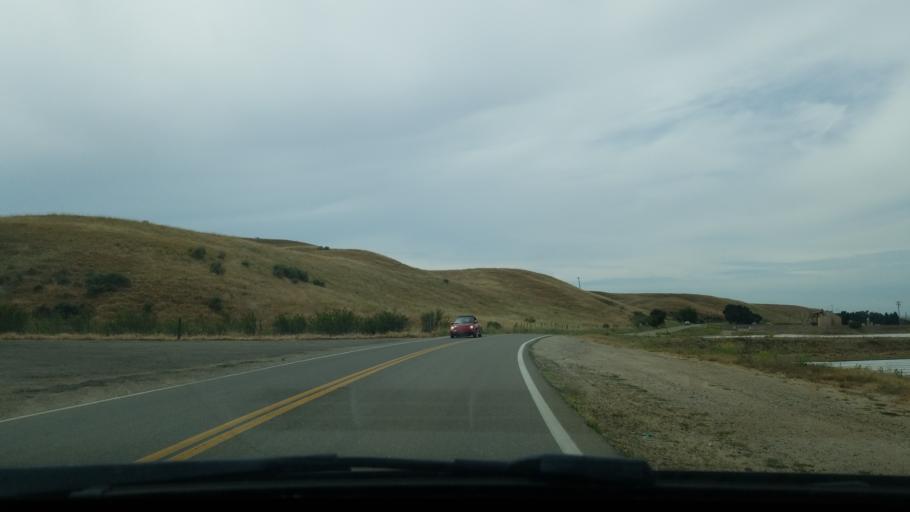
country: US
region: California
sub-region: Santa Barbara County
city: Orcutt
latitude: 34.8733
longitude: -120.3070
